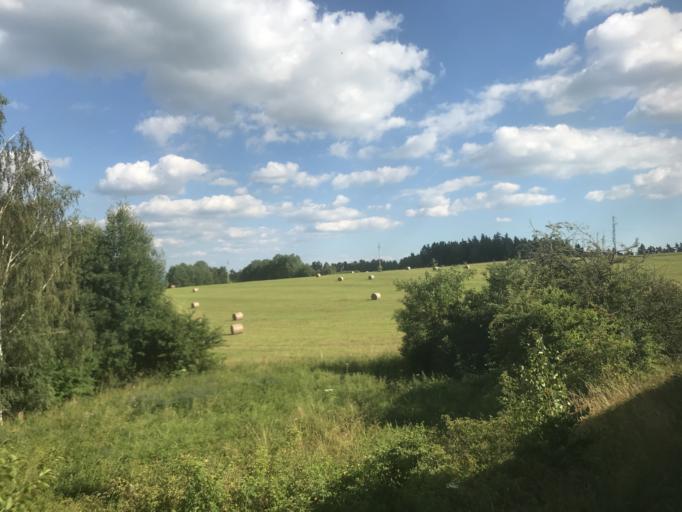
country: CZ
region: Jihocesky
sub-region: Okres Cesky Krumlov
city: Dolni Dvoriste
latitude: 48.6630
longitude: 14.4379
